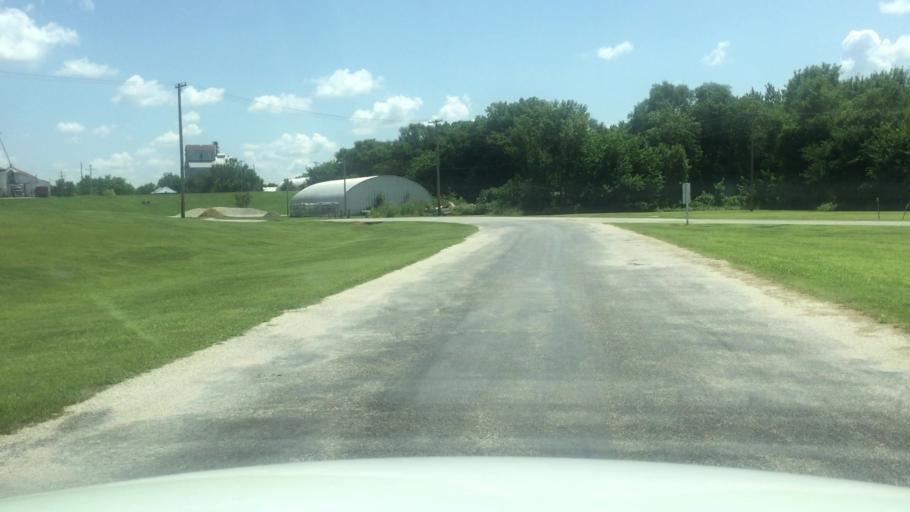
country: US
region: Kansas
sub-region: Brown County
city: Horton
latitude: 39.6563
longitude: -95.5283
